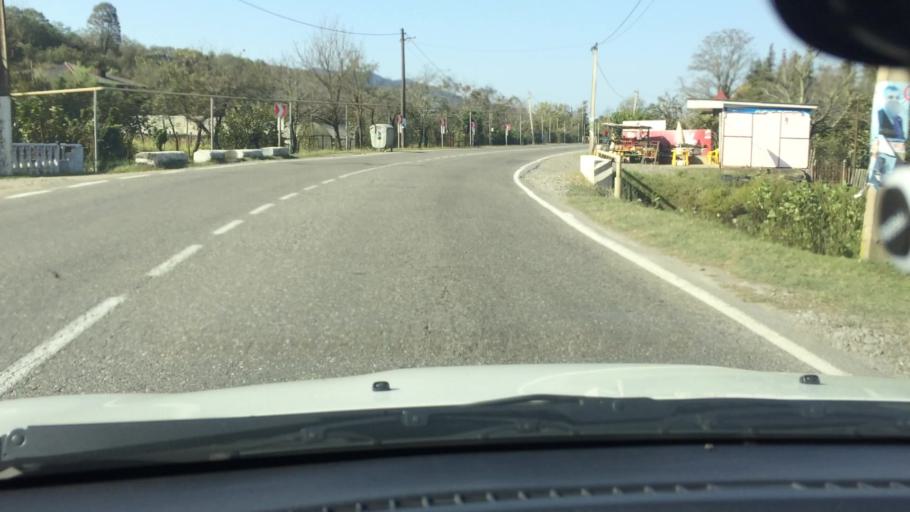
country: GE
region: Guria
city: Lanchkhuti
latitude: 42.0856
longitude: 42.1151
